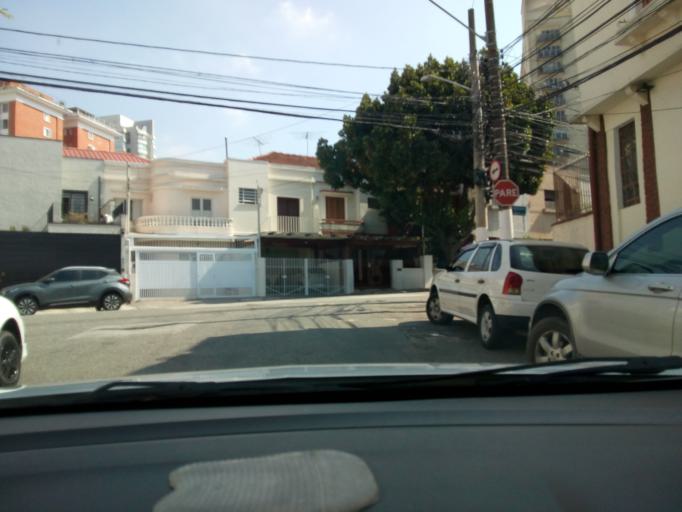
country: BR
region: Sao Paulo
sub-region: Sao Paulo
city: Sao Paulo
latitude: -23.5866
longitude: -46.6381
